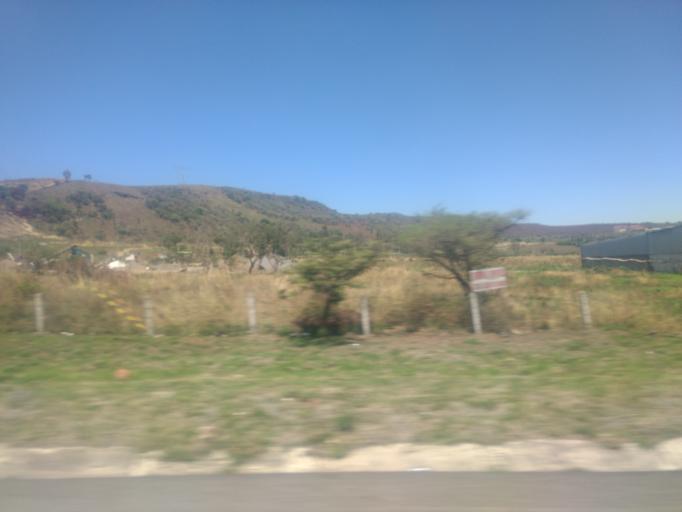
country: MX
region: Jalisco
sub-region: Acatlan de Juarez
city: Villa de los Ninos
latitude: 20.4222
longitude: -103.5551
